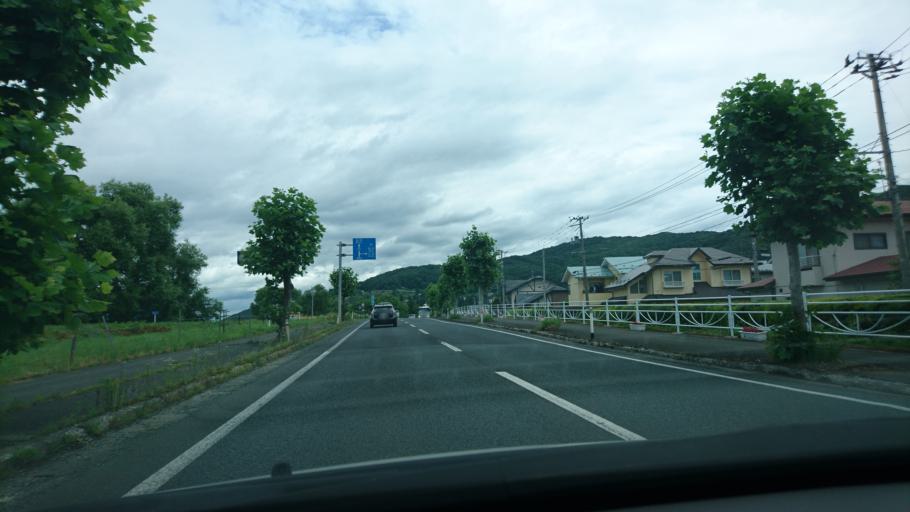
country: JP
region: Iwate
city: Morioka-shi
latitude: 39.6528
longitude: 141.1825
